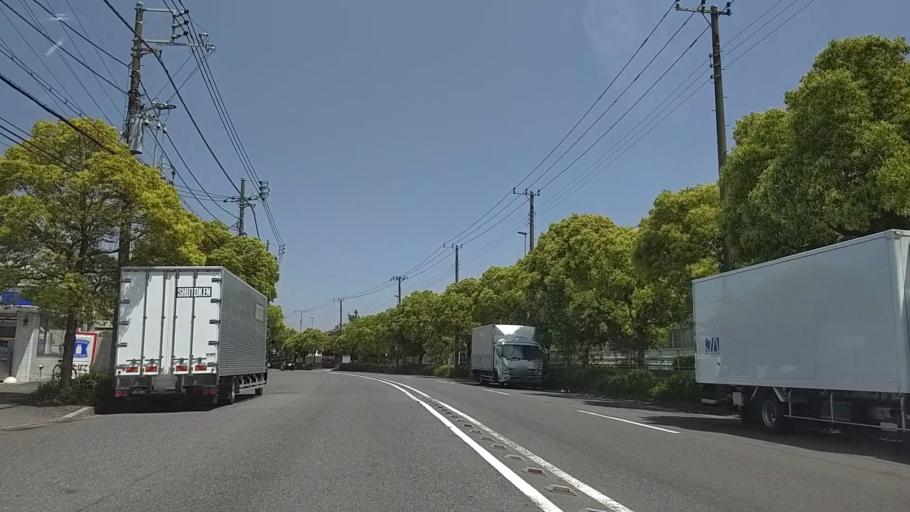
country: JP
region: Kanagawa
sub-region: Kawasaki-shi
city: Kawasaki
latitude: 35.5234
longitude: 139.7463
